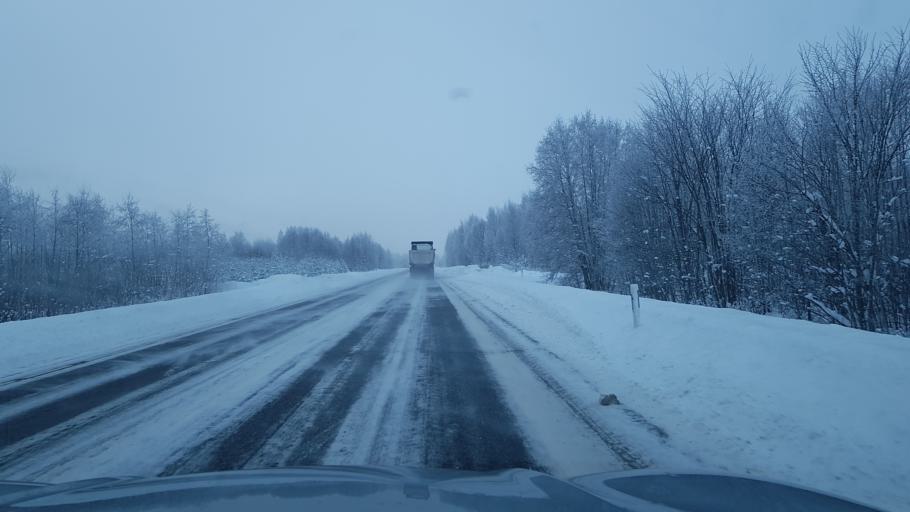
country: EE
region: Ida-Virumaa
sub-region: Johvi vald
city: Johvi
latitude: 59.2174
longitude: 27.3386
